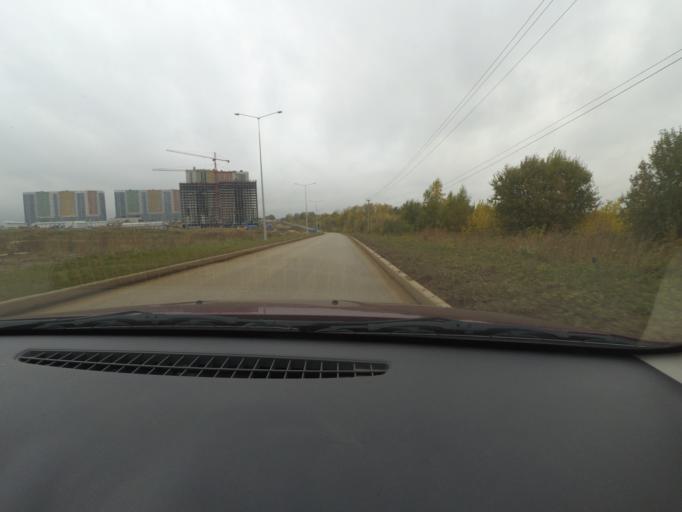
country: RU
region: Nizjnij Novgorod
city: Afonino
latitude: 56.2475
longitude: 44.0541
